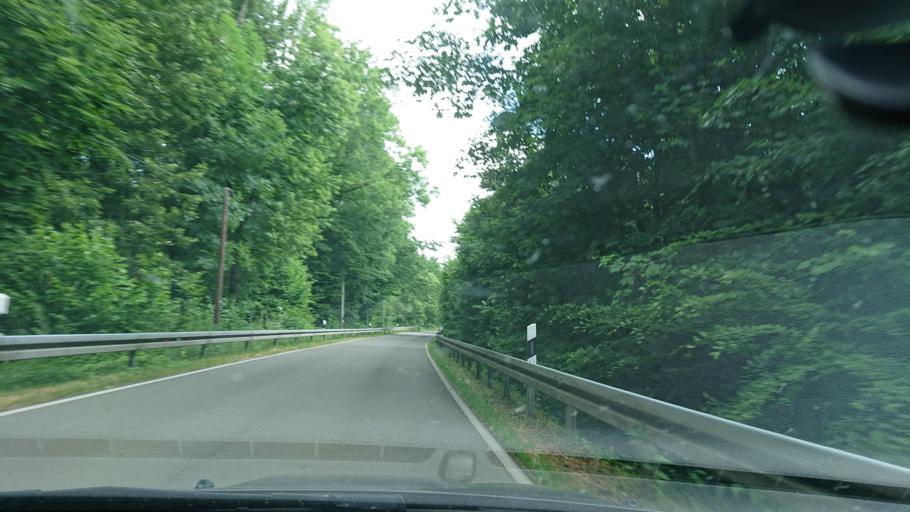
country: DE
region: North Rhine-Westphalia
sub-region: Regierungsbezirk Detmold
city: Rodinghausen
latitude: 52.2594
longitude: 8.4486
